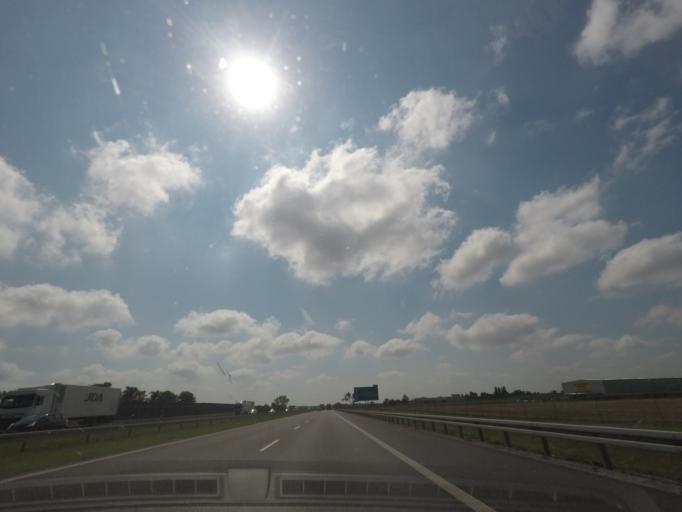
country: PL
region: Kujawsko-Pomorskie
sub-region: Powiat wloclawski
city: Brzesc Kujawski
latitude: 52.6342
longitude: 18.9543
